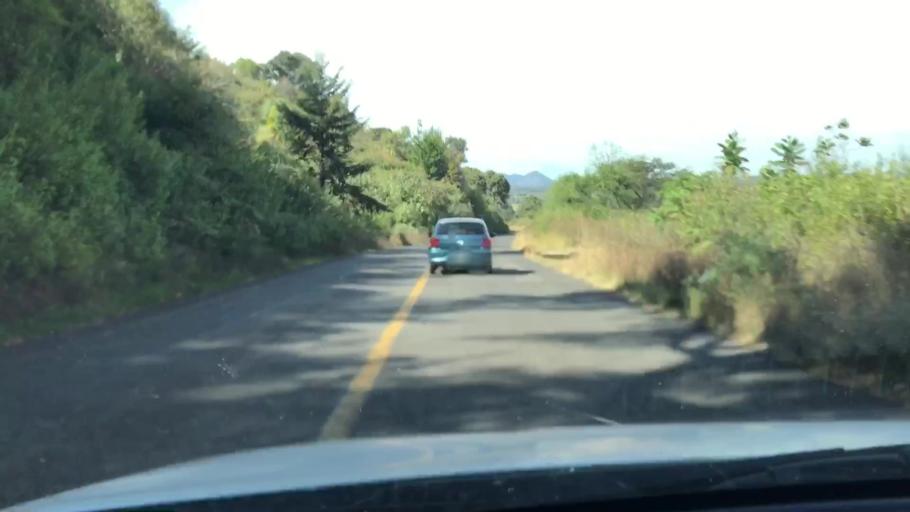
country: MX
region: Jalisco
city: Chiquilistlan
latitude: 20.1419
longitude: -103.7211
